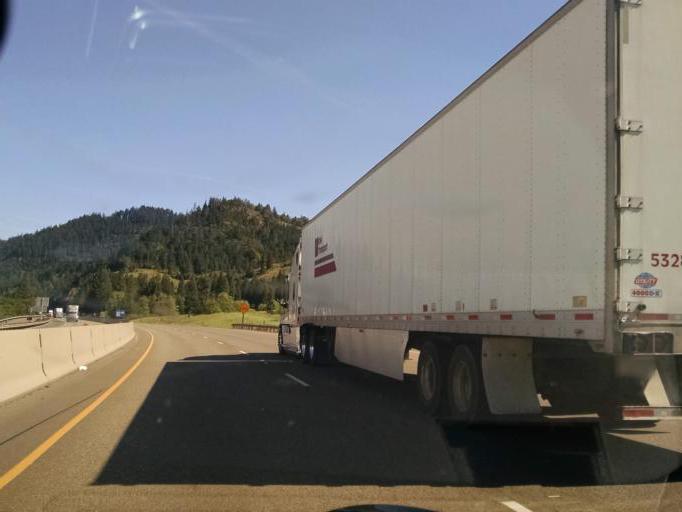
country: US
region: Oregon
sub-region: Douglas County
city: Myrtle Creek
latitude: 43.0352
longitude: -123.3302
